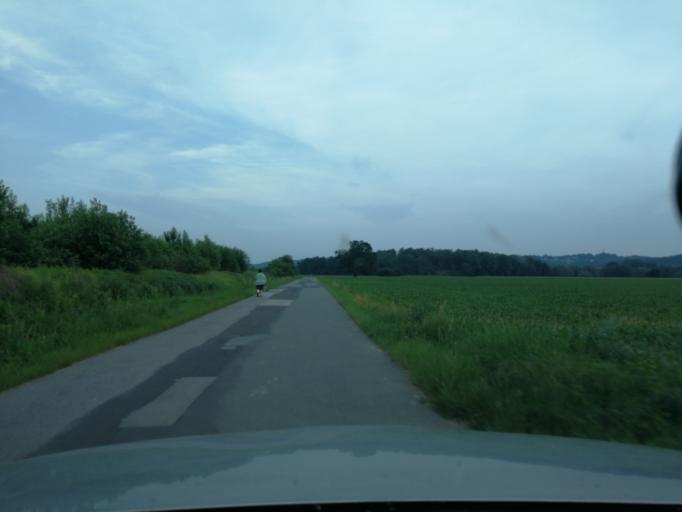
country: AT
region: Burgenland
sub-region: Politischer Bezirk Jennersdorf
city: Konigsdorf
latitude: 47.0126
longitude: 16.1547
